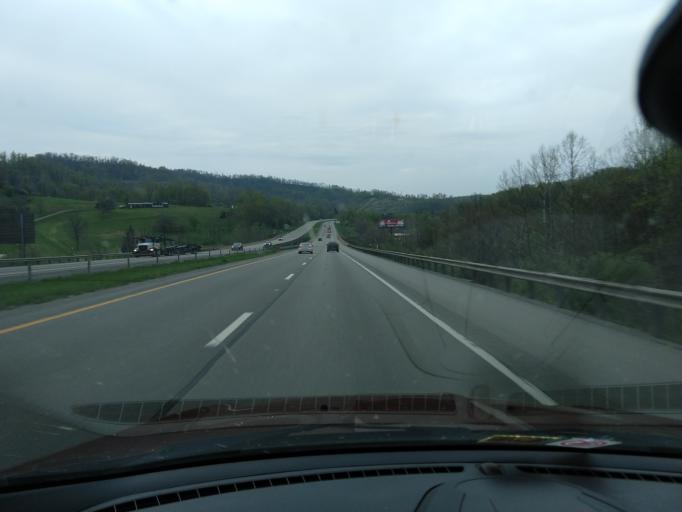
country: US
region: West Virginia
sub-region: Lewis County
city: Weston
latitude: 39.1206
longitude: -80.3869
